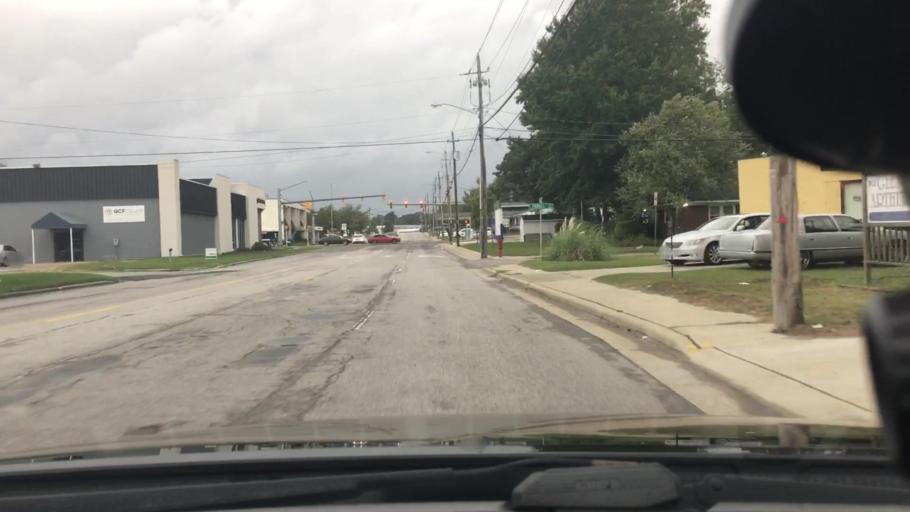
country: US
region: North Carolina
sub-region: Pitt County
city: Greenville
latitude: 35.6016
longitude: -77.3739
